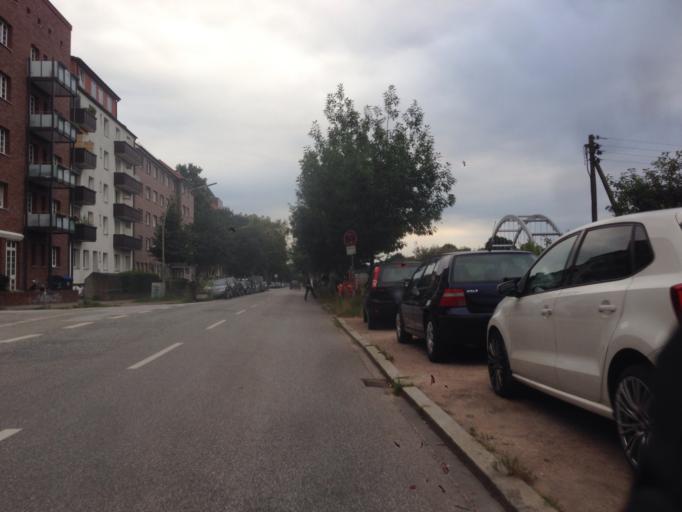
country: DE
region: Hamburg
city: Barmbek-Nord
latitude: 53.5950
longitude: 10.0376
